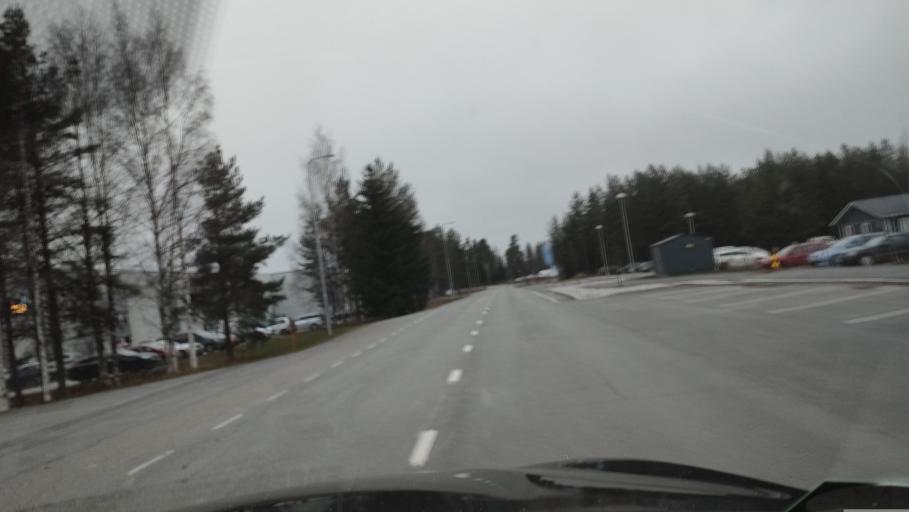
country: FI
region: Southern Ostrobothnia
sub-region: Suupohja
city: Kauhajoki
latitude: 62.4591
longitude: 22.2014
